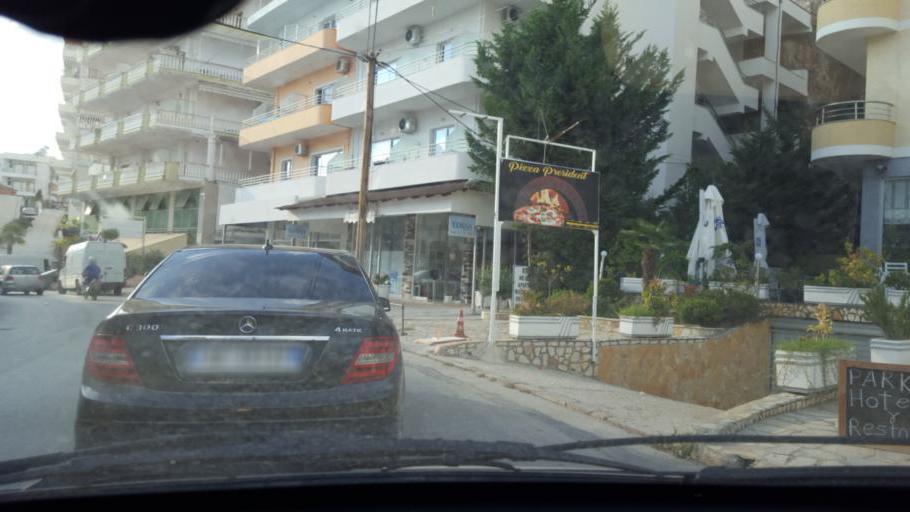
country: AL
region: Vlore
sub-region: Rrethi i Sarandes
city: Sarande
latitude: 39.8637
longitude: 20.0192
